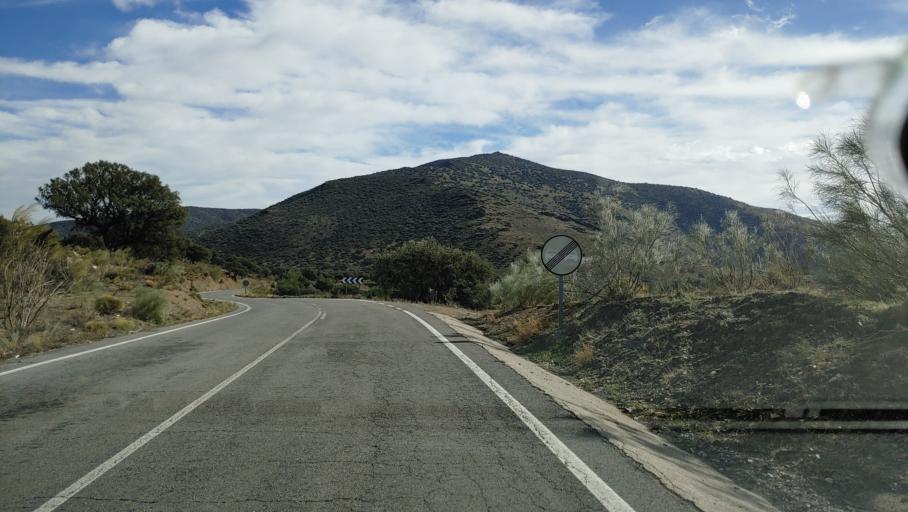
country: ES
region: Andalusia
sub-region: Provincia de Almeria
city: Ohanes
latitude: 37.0861
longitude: -2.7410
